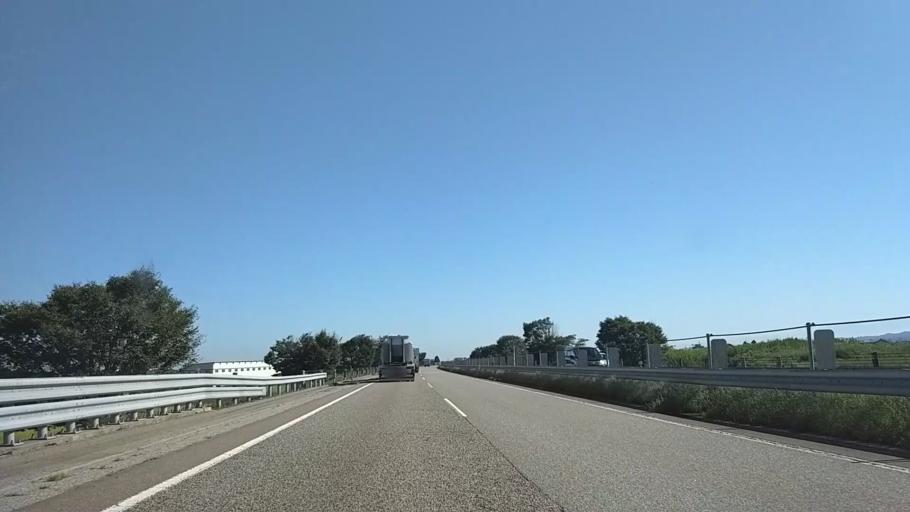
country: JP
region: Toyama
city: Nanto-shi
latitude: 36.6428
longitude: 136.9765
